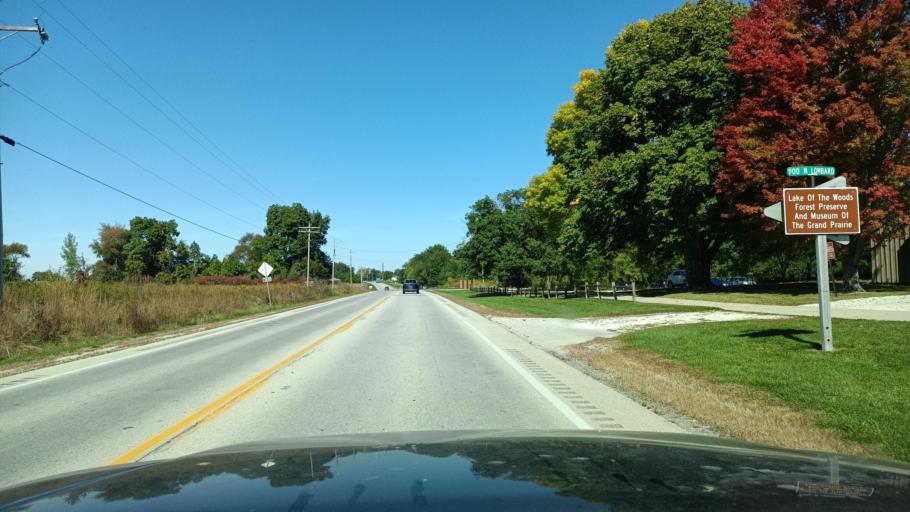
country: US
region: Illinois
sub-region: Champaign County
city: Mahomet
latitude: 40.2051
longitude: -88.3946
